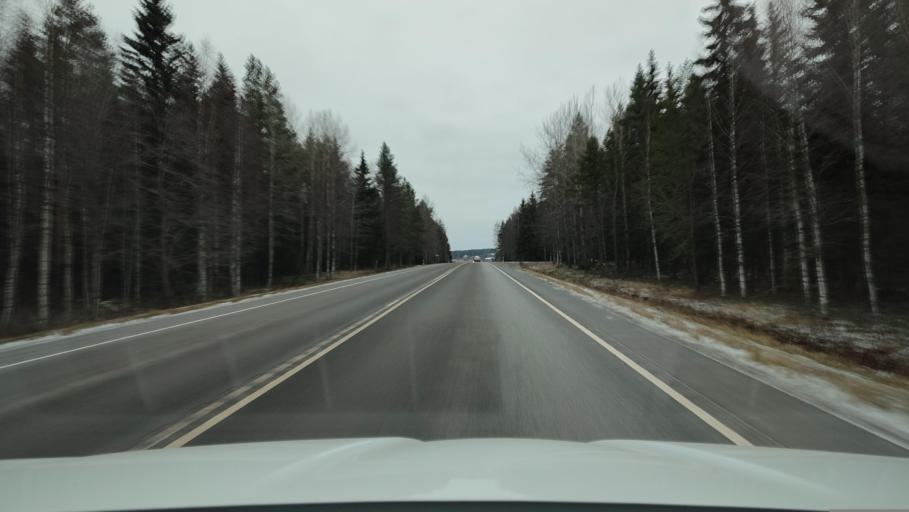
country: FI
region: Ostrobothnia
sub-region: Vaasa
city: Ristinummi
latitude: 62.9381
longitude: 21.7546
